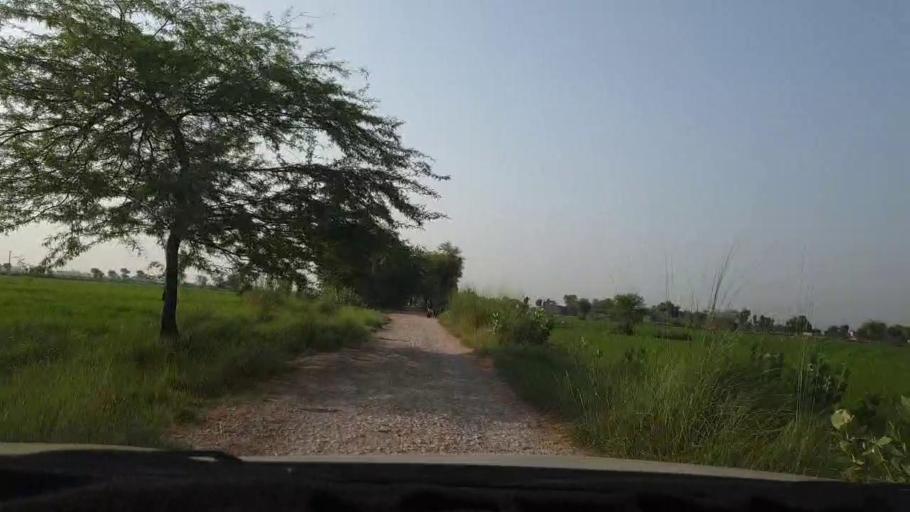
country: PK
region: Sindh
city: Larkana
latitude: 27.5059
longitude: 68.1740
